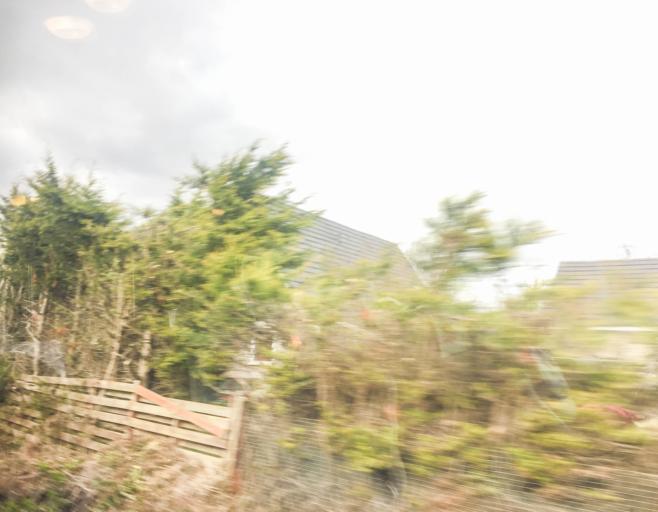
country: GB
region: Scotland
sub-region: Argyll and Bute
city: Cardross
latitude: 55.9609
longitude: -4.6547
